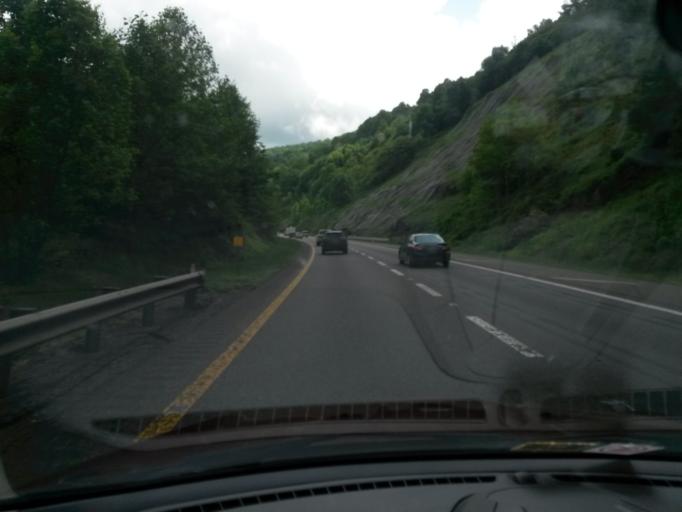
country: US
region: Virginia
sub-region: Carroll County
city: Cana
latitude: 36.6154
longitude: -80.7404
